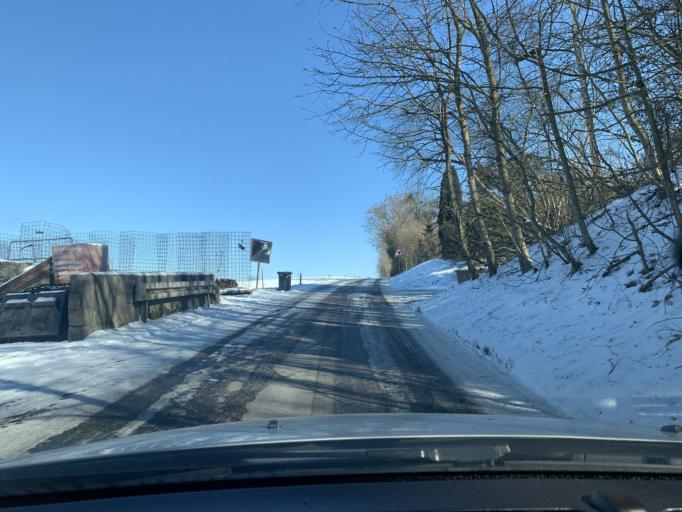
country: DE
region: Bavaria
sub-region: Upper Bavaria
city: Lohkirchen
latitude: 48.3209
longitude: 12.4668
